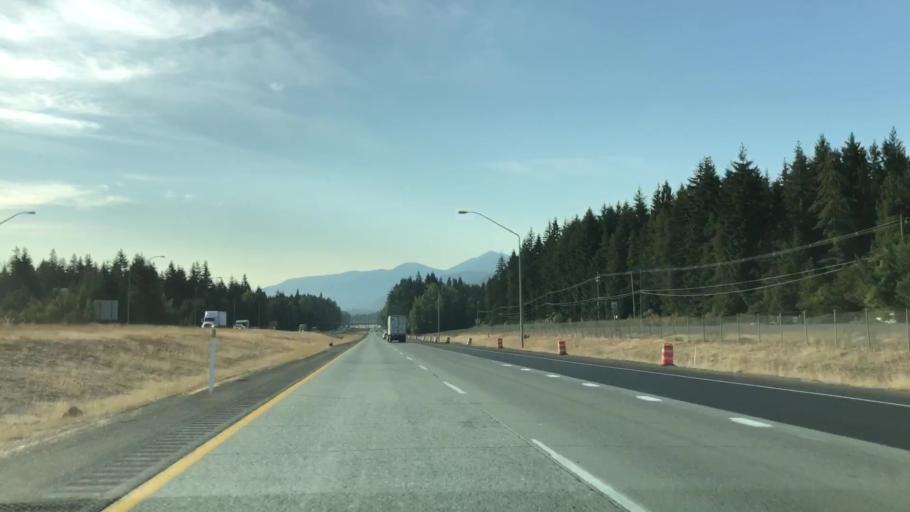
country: US
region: Washington
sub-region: Kittitas County
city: Cle Elum
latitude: 47.2455
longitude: -121.1856
